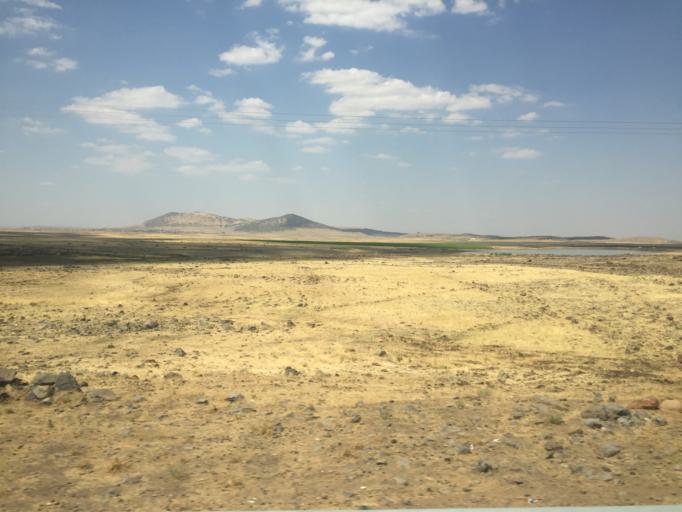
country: TR
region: Sanliurfa
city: Karacadag
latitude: 37.8506
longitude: 39.7180
